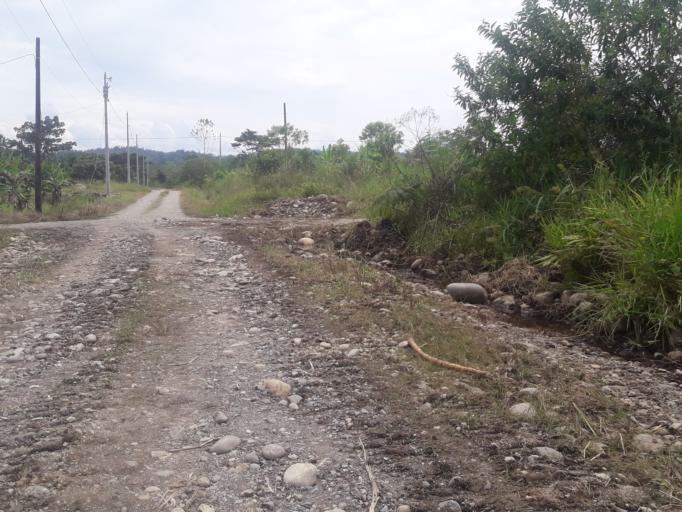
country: EC
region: Napo
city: Tena
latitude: -1.0603
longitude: -77.7958
